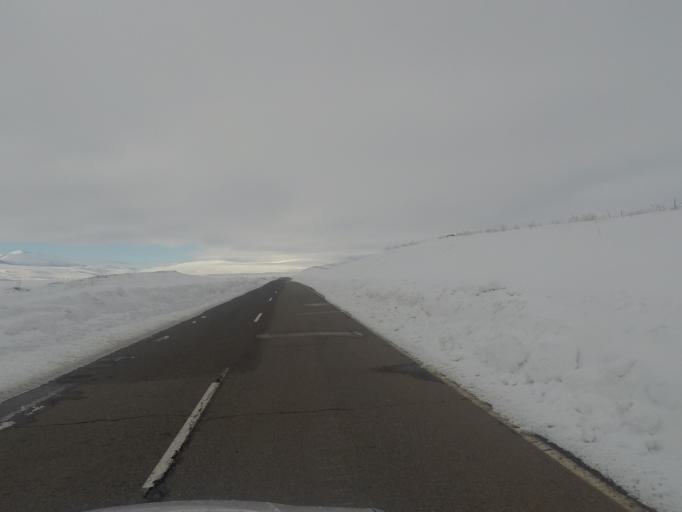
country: GE
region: Samtskhe-Javakheti
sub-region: Ninotsminda
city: Ninotsminda
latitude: 41.4178
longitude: 43.8333
